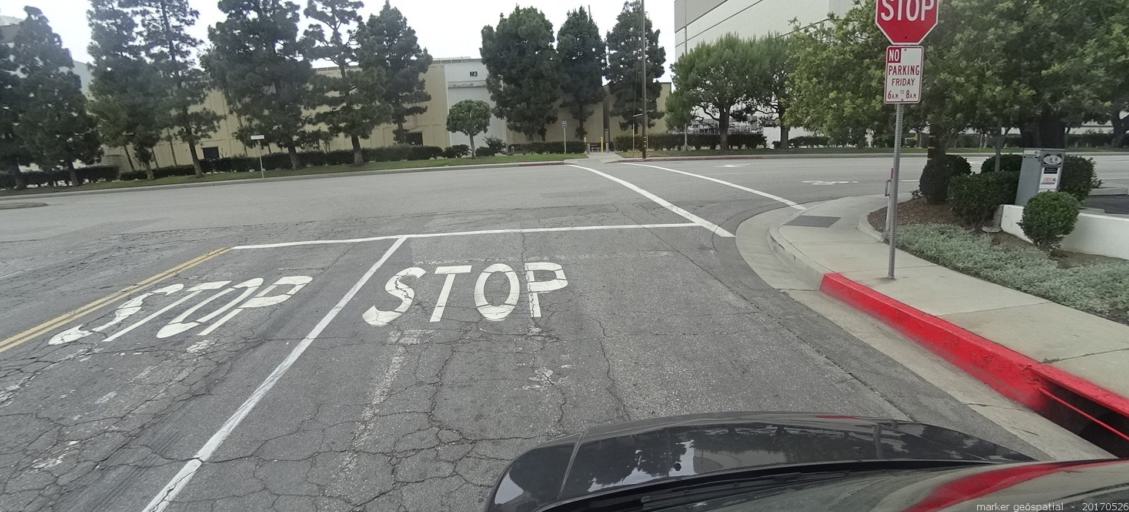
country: US
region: California
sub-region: Los Angeles County
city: Lawndale
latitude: 33.8898
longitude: -118.3698
